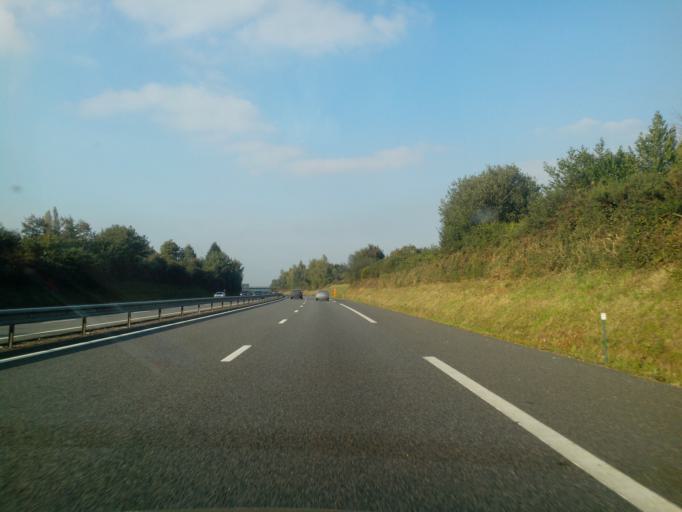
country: FR
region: Brittany
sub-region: Departement du Morbihan
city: Malestroit
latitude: 47.8644
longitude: -2.4169
